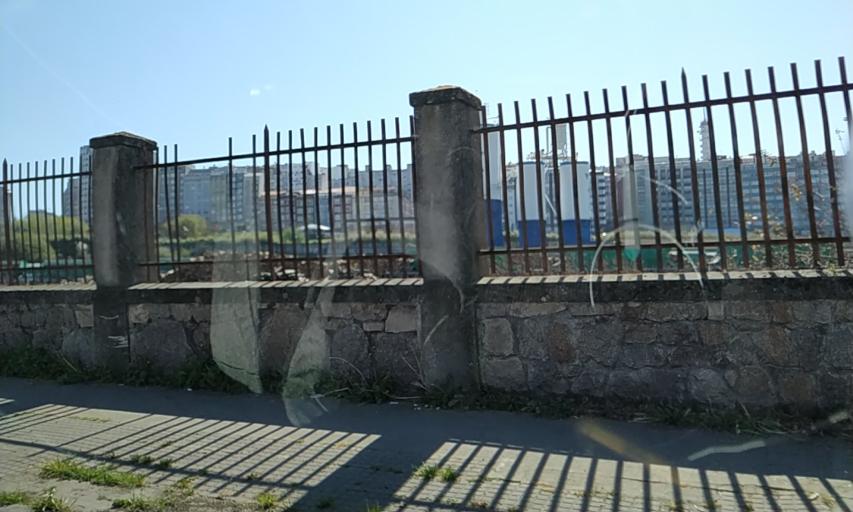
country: ES
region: Galicia
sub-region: Provincia da Coruna
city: A Coruna
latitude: 43.3565
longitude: -8.3932
